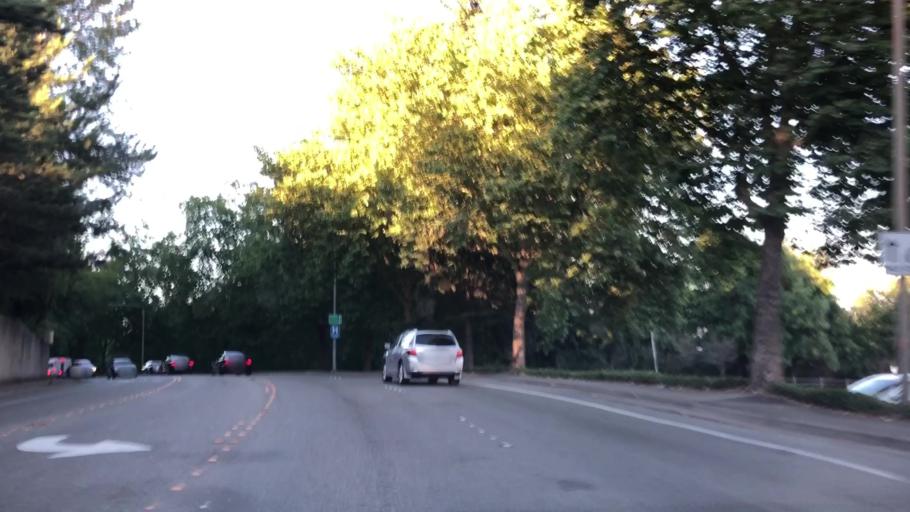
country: US
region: Washington
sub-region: King County
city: Redmond
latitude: 47.6731
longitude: -122.1104
